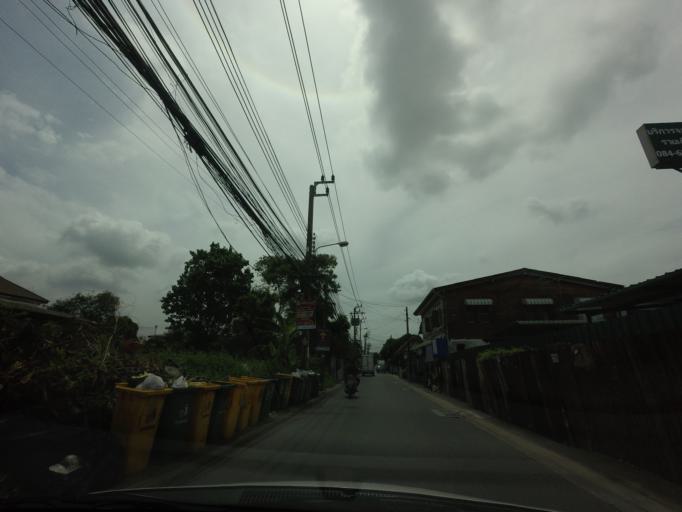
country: TH
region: Bangkok
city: Thung Khru
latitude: 13.6428
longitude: 100.5060
